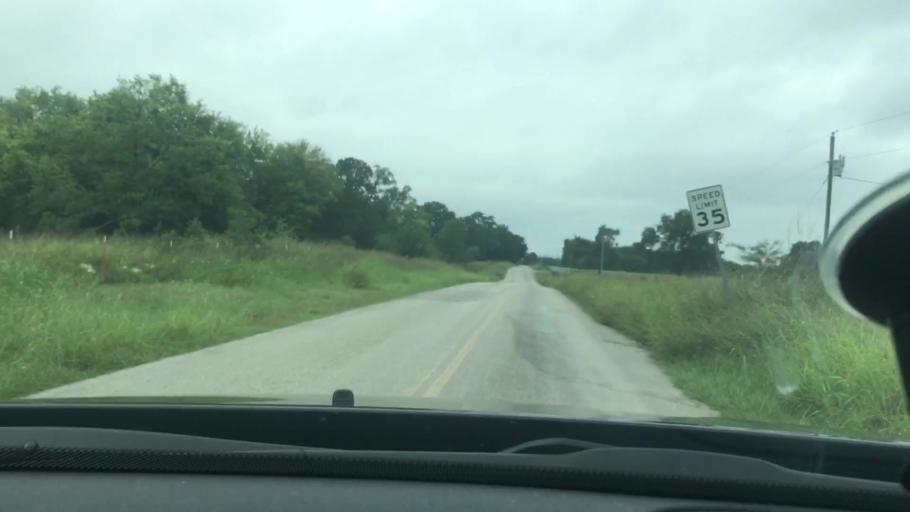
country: US
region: Oklahoma
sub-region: Pontotoc County
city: Ada
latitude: 34.8108
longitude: -96.7573
